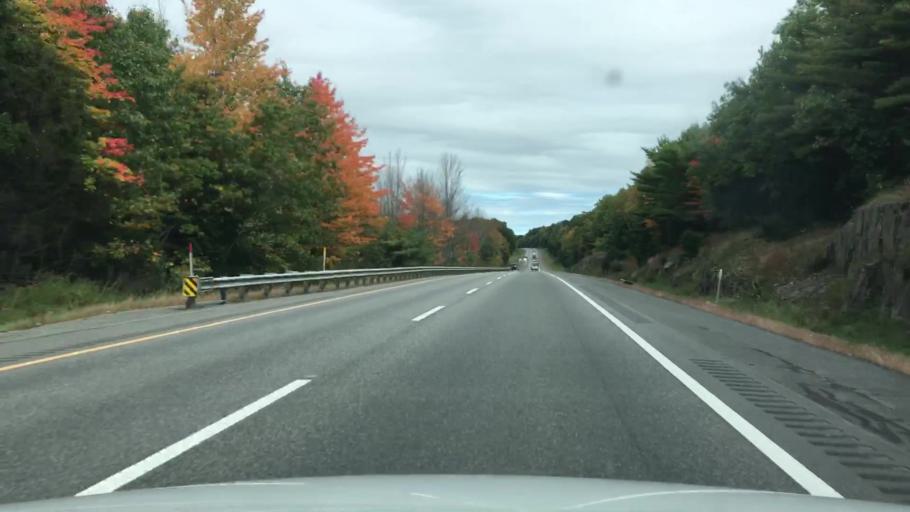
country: US
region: Maine
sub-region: Kennebec County
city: Sidney
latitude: 44.3891
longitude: -69.7601
